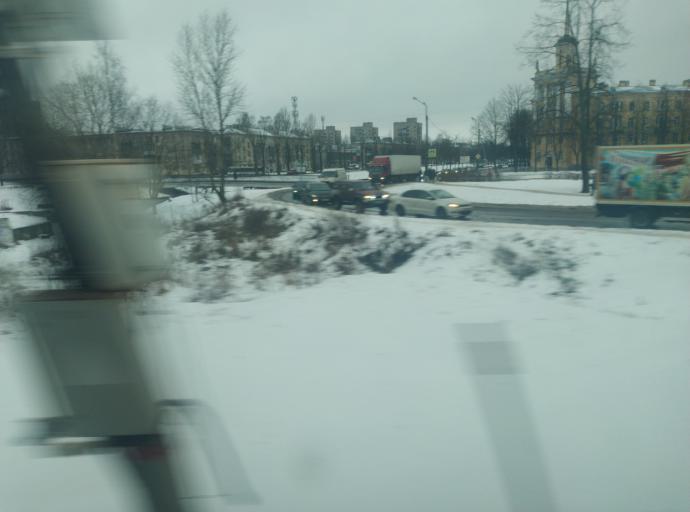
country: RU
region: St.-Petersburg
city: Kolpino
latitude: 59.7484
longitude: 30.6164
